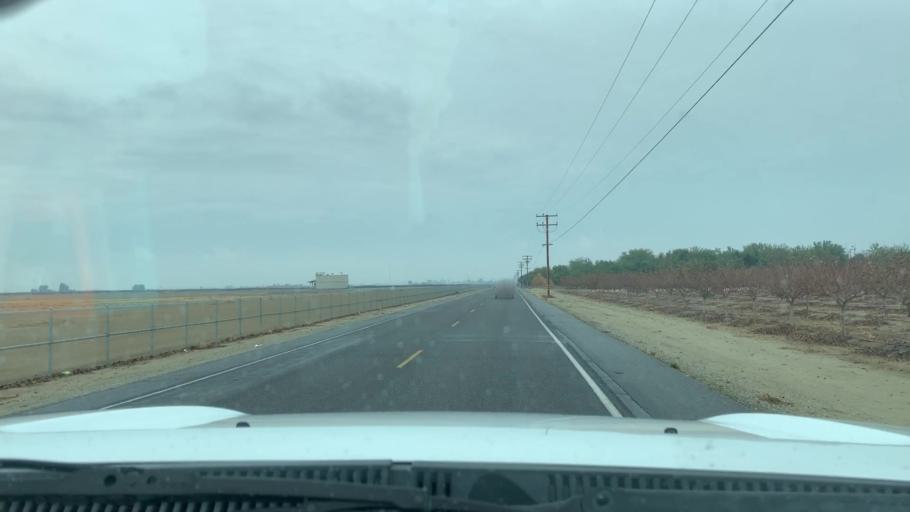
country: US
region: California
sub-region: Kern County
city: Delano
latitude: 35.7613
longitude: -119.3227
